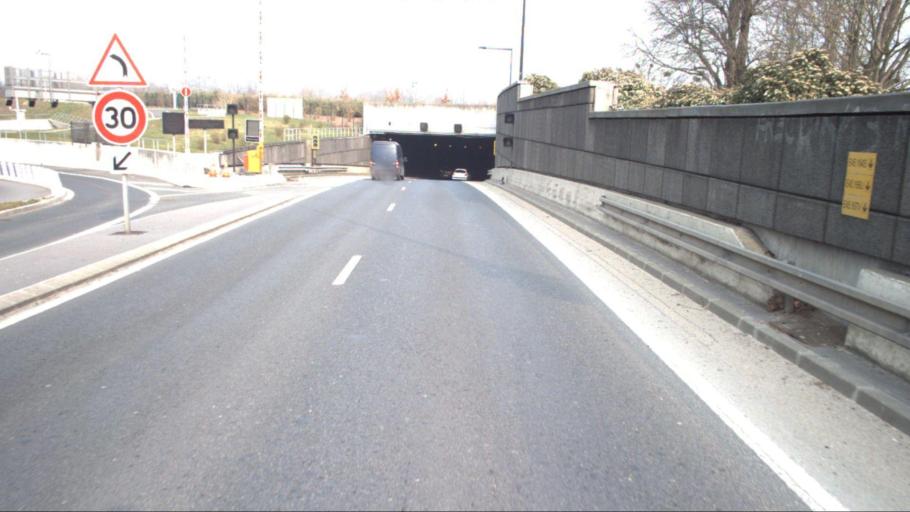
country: FR
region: Ile-de-France
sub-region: Departement des Yvelines
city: Chatou
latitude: 48.8715
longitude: 2.1582
